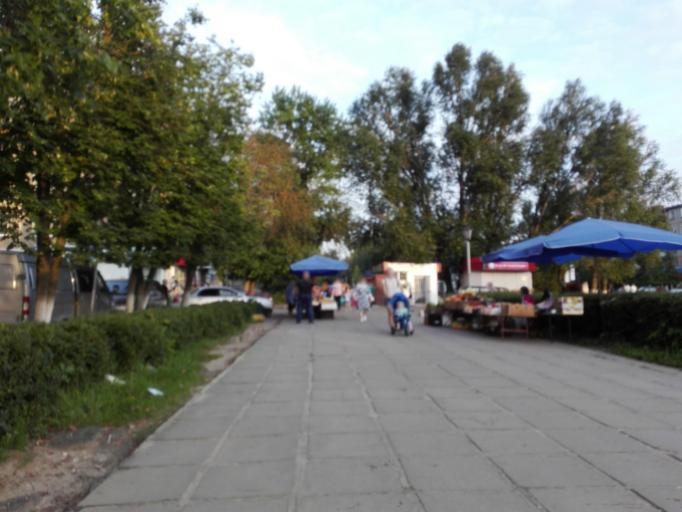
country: RU
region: Orjol
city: Orel
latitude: 53.0137
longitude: 36.1424
